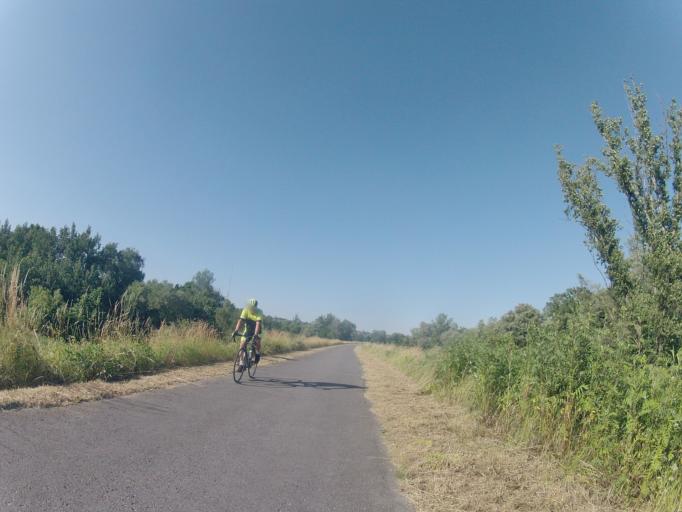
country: PL
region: Lesser Poland Voivodeship
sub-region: Krakow
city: Krakow
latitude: 50.0438
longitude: 19.8991
